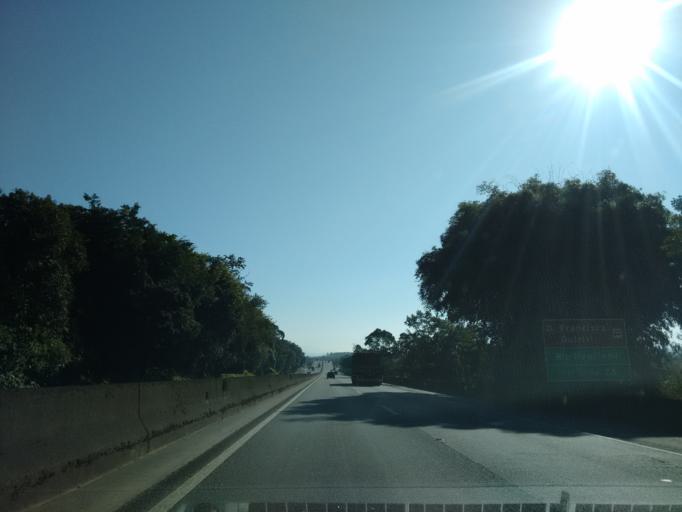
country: BR
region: Santa Catarina
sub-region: Joinville
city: Joinville
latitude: -26.2090
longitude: -48.9153
